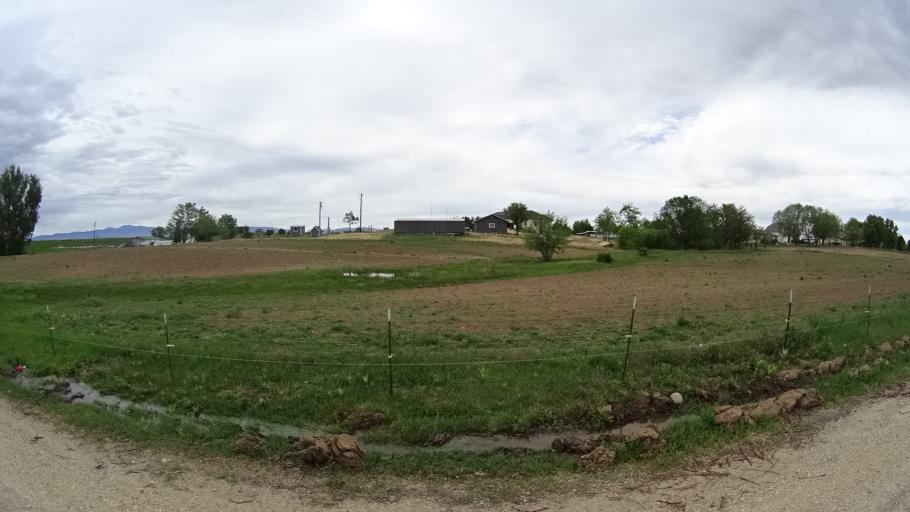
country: US
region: Idaho
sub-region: Ada County
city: Meridian
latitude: 43.5598
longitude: -116.4139
